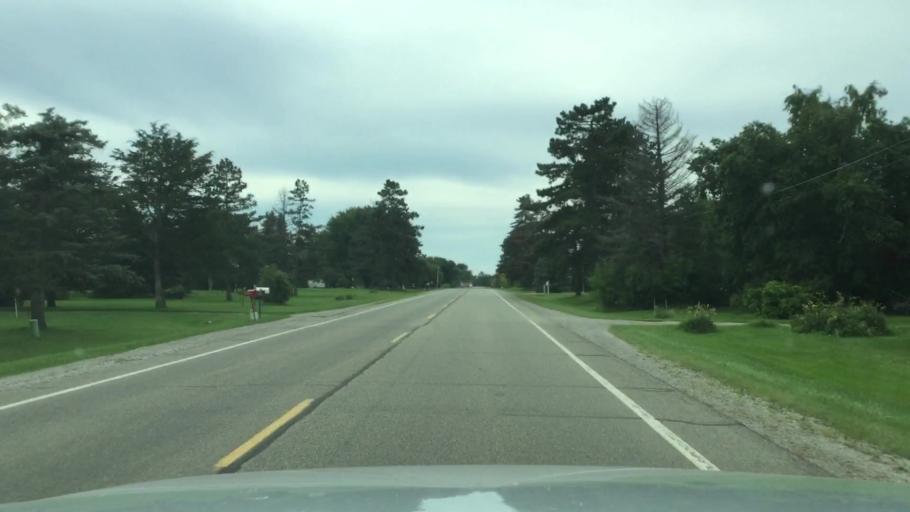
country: US
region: Michigan
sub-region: Shiawassee County
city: Durand
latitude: 42.9302
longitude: -83.9555
